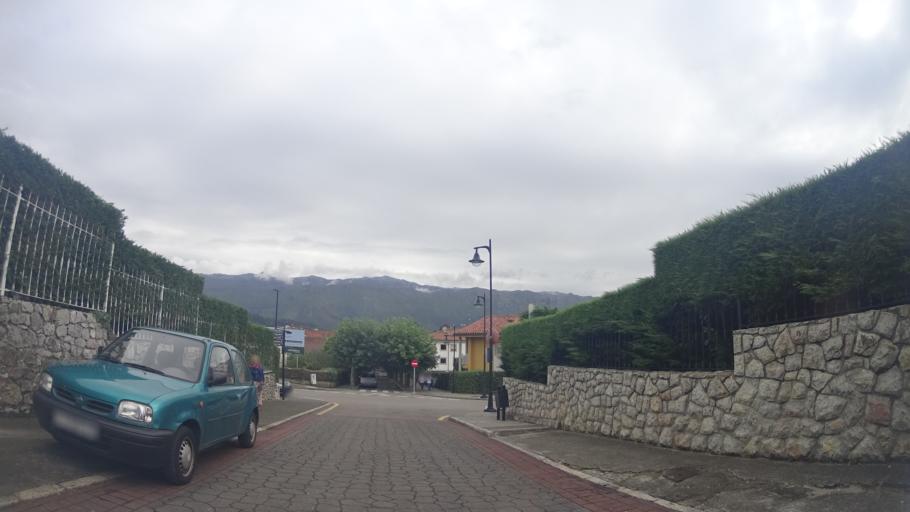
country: ES
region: Asturias
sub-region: Province of Asturias
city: Llanes
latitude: 43.4243
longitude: -4.7563
